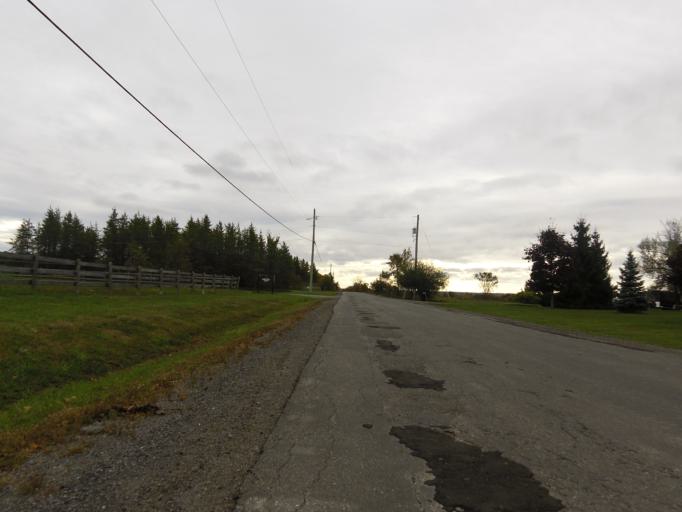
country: CA
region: Ontario
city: Arnprior
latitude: 45.4700
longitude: -76.1544
